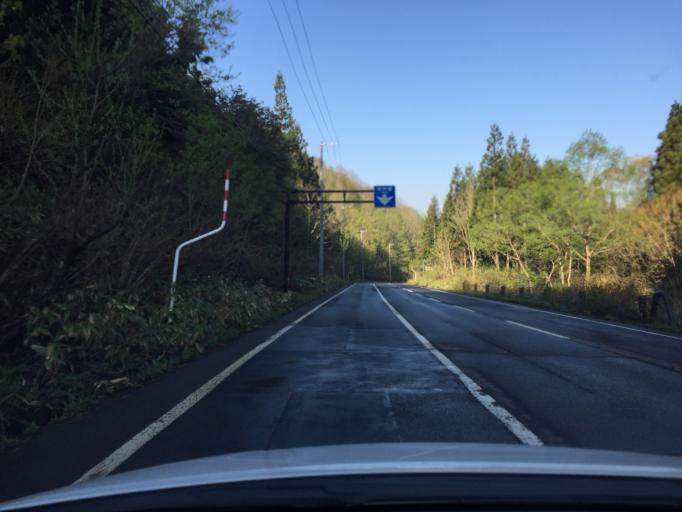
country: JP
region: Fukushima
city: Inawashiro
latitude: 37.6609
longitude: 140.0257
